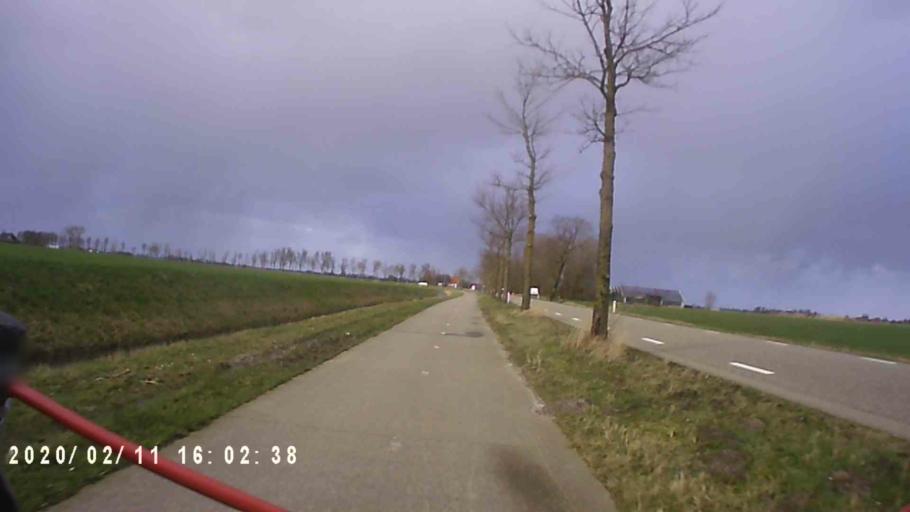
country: NL
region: Groningen
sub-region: Gemeente Zuidhorn
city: Oldehove
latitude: 53.2996
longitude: 6.4205
